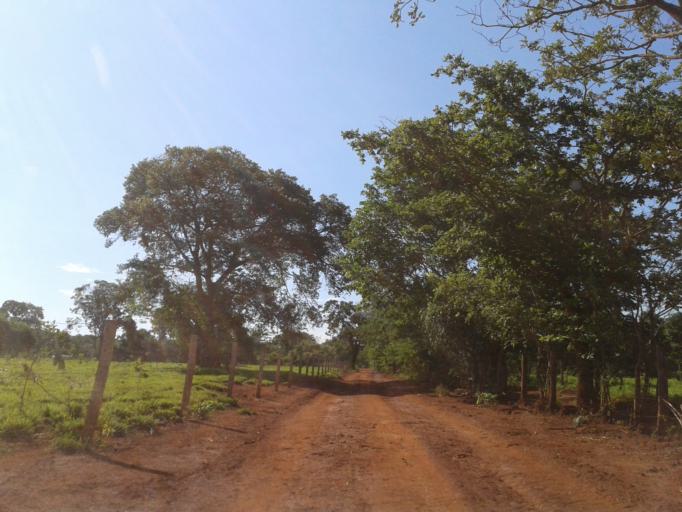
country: BR
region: Minas Gerais
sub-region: Santa Vitoria
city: Santa Vitoria
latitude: -19.1162
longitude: -50.5406
